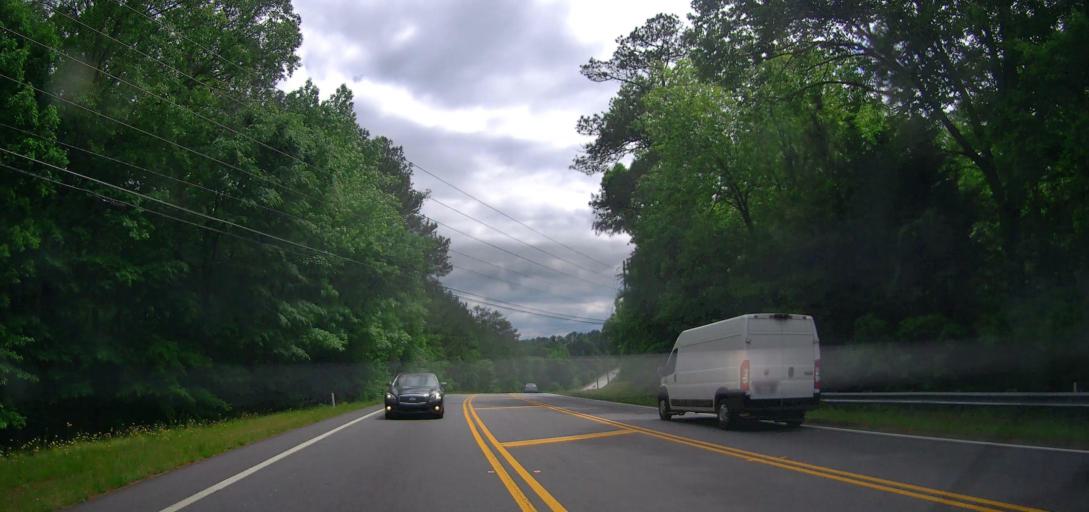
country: US
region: Georgia
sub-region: DeKalb County
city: Pine Mountain
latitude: 33.6051
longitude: -84.0955
